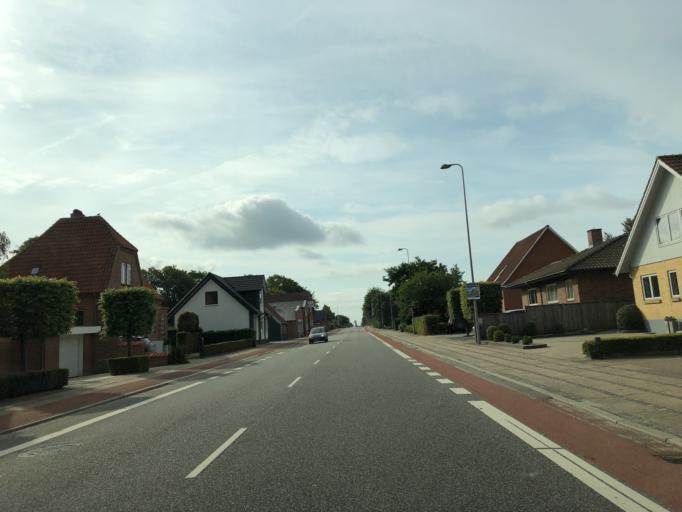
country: DK
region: Central Jutland
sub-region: Ringkobing-Skjern Kommune
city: Skjern
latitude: 55.9421
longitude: 8.4991
